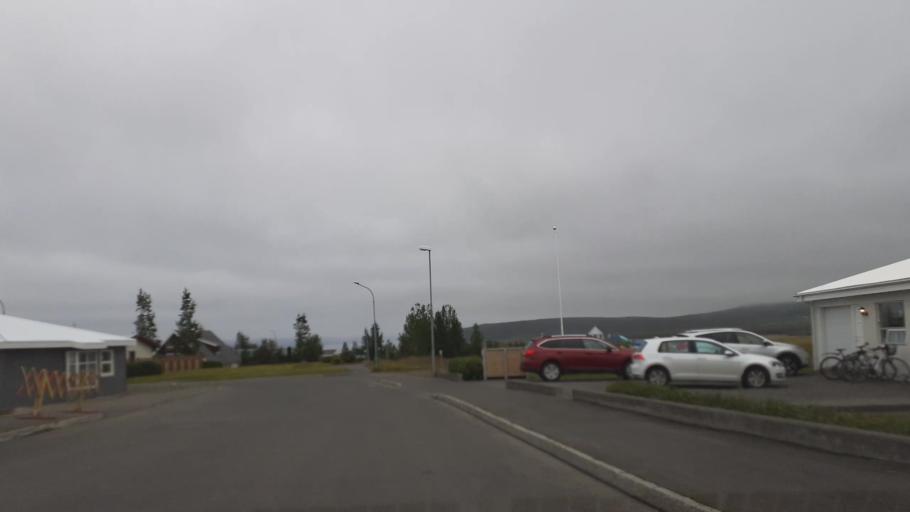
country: IS
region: Northeast
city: Dalvik
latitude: 65.9679
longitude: -18.5422
